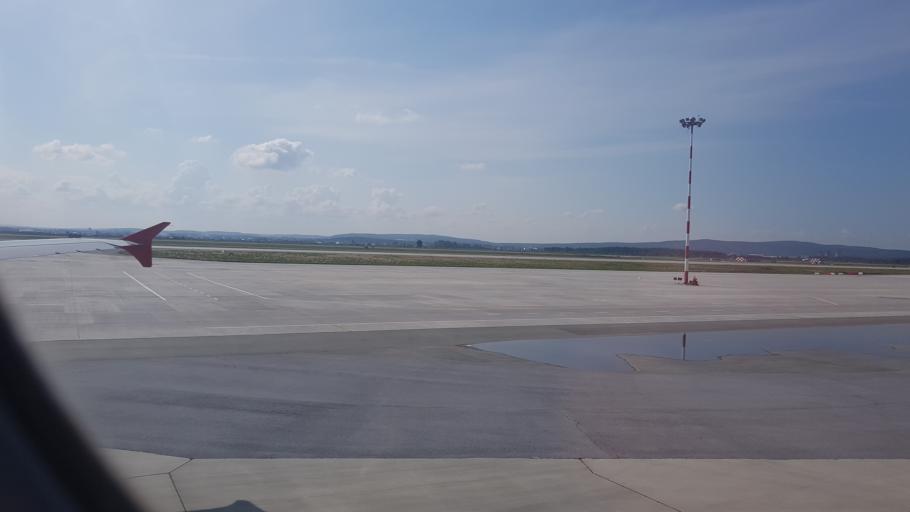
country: RU
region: Sverdlovsk
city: Istok
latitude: 56.7486
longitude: 60.8004
